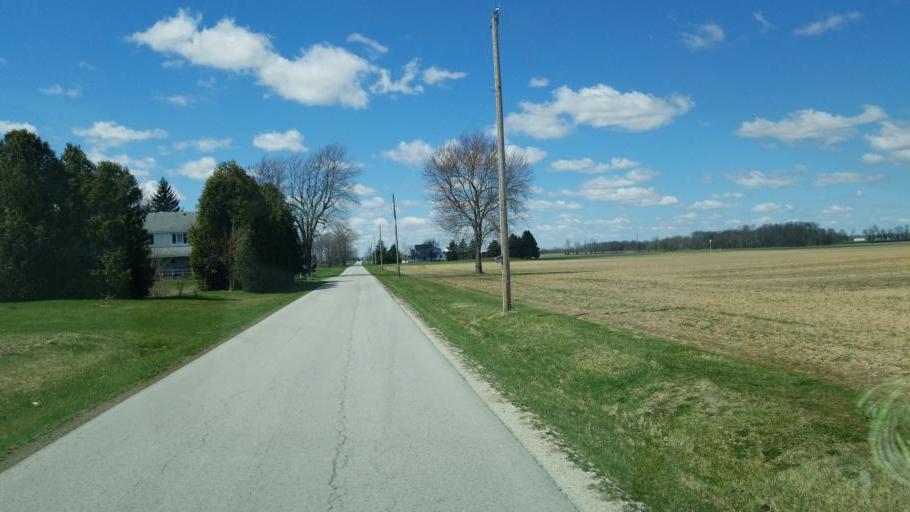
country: US
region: Ohio
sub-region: Seneca County
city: Fostoria
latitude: 41.0938
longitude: -83.4989
